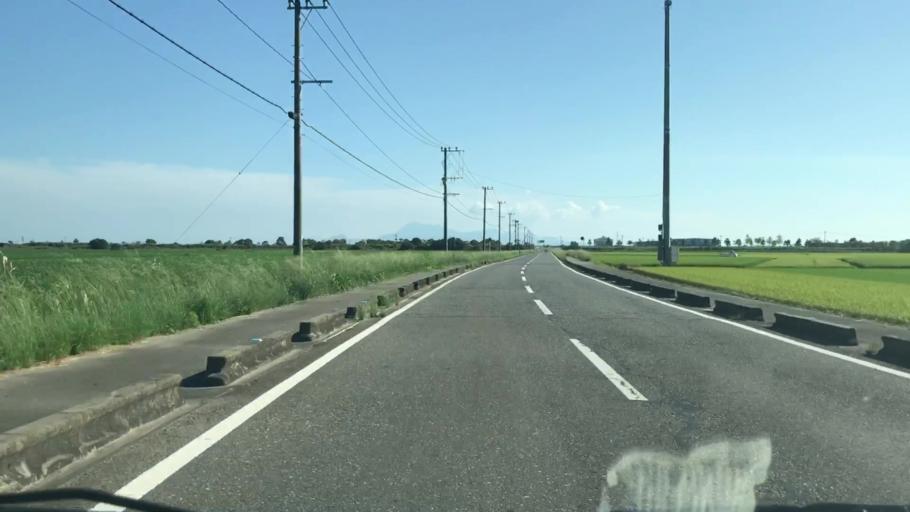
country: JP
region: Saga Prefecture
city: Okawa
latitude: 33.1588
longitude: 130.3086
